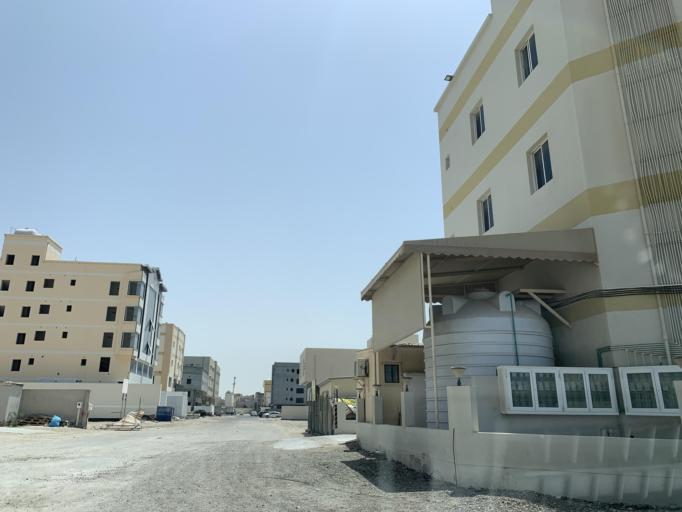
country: BH
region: Northern
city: Madinat `Isa
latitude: 26.1922
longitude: 50.5484
